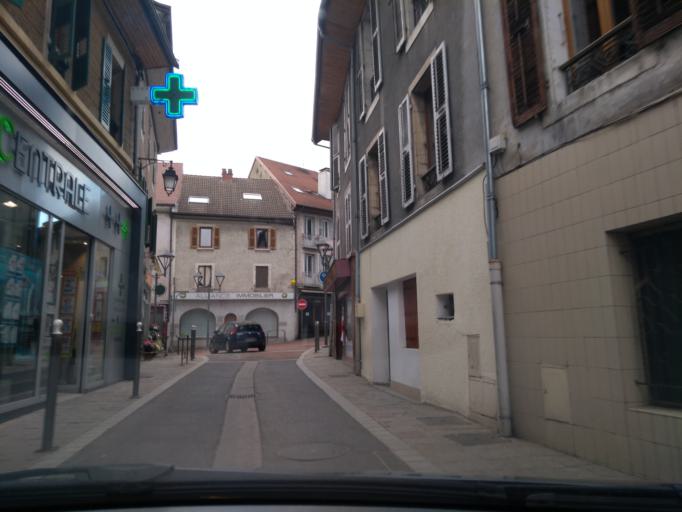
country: FR
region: Rhone-Alpes
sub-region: Departement de la Haute-Savoie
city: Rumilly
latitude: 45.8680
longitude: 5.9436
